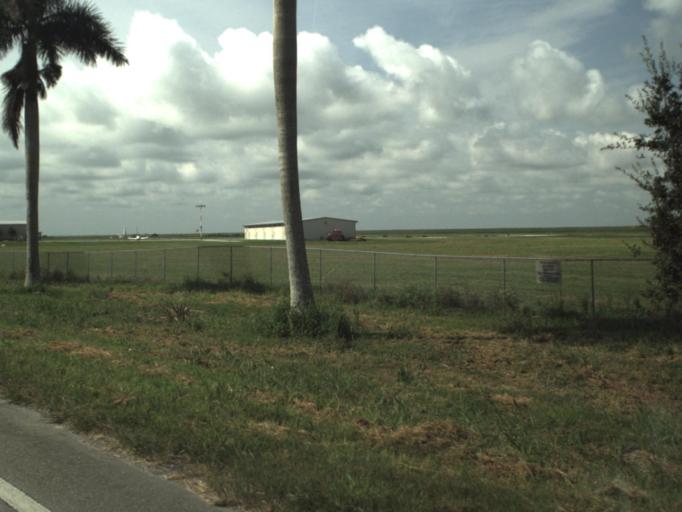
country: US
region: Florida
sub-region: Palm Beach County
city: Pahokee
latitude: 26.7920
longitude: -80.6921
